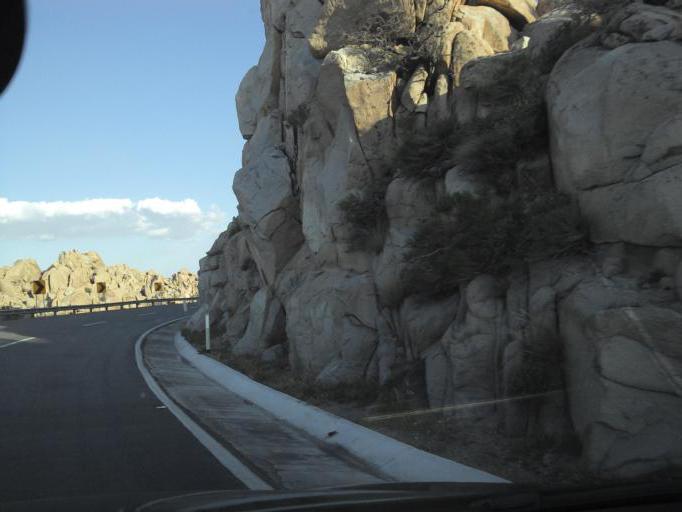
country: MX
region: Baja California
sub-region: Tecate
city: Cereso del Hongo
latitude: 32.5801
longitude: -116.0284
